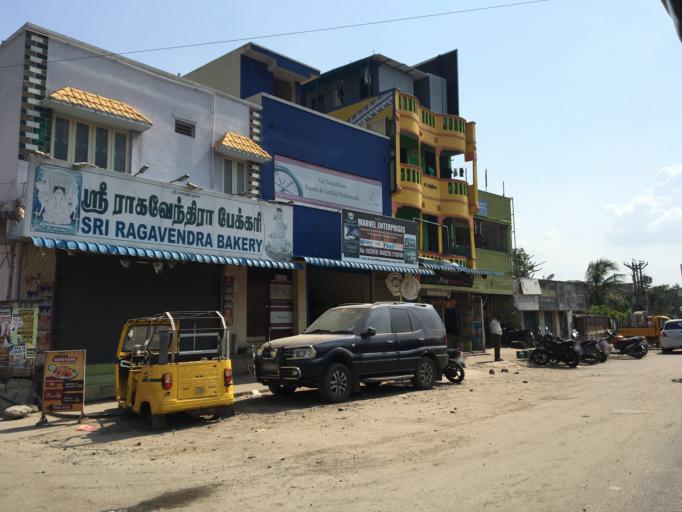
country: IN
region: Tamil Nadu
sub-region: Kancheepuram
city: Perungudi
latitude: 12.9807
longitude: 80.2496
